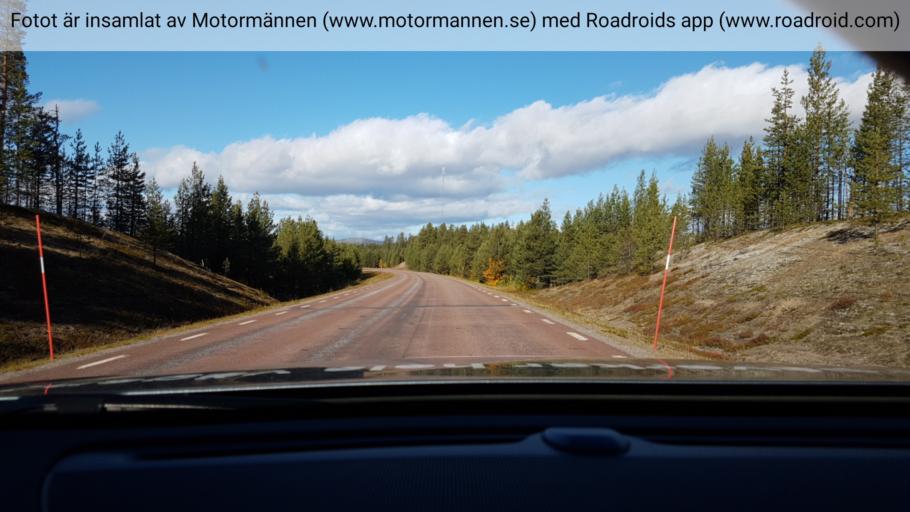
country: SE
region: Norrbotten
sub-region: Arjeplogs Kommun
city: Arjeplog
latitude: 66.0447
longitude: 18.0350
